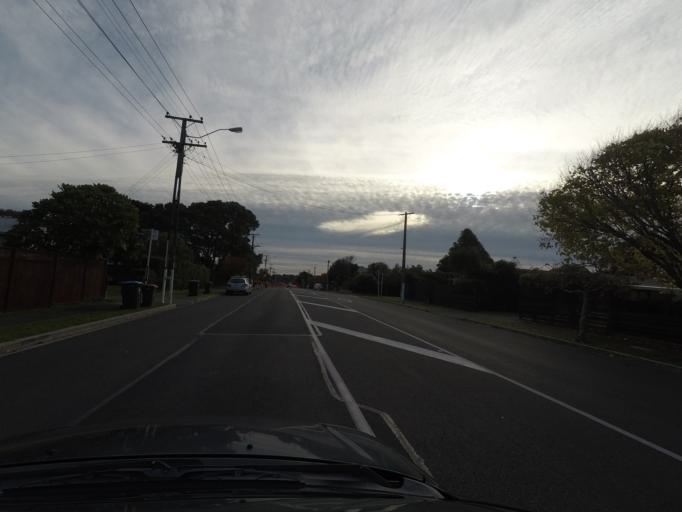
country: NZ
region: Auckland
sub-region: Auckland
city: Tamaki
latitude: -36.8917
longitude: 174.8238
